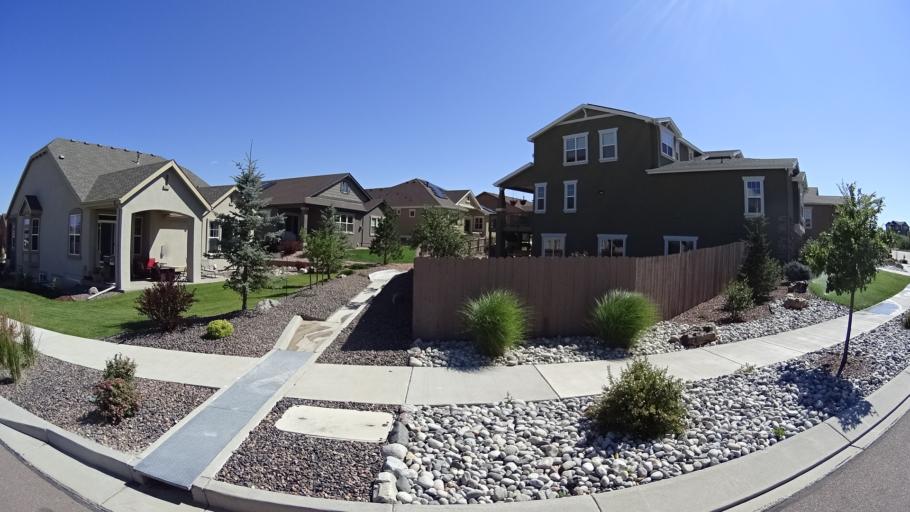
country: US
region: Colorado
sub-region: El Paso County
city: Black Forest
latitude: 38.9783
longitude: -104.7428
